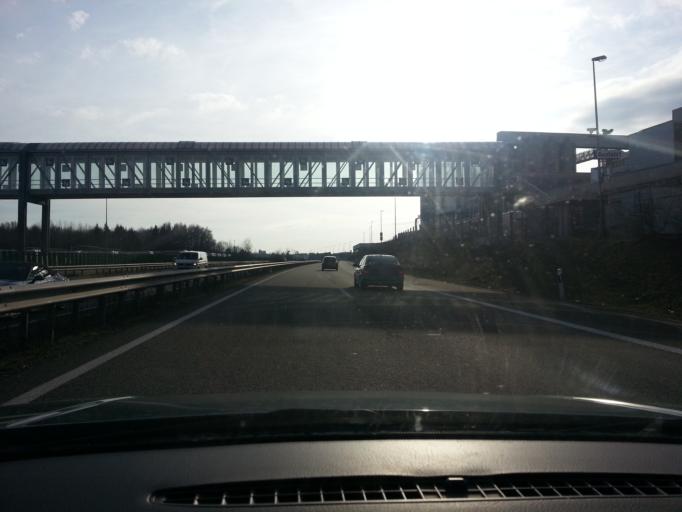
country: DE
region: Rheinland-Pfalz
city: Pirmasens
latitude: 49.2227
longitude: 7.5961
